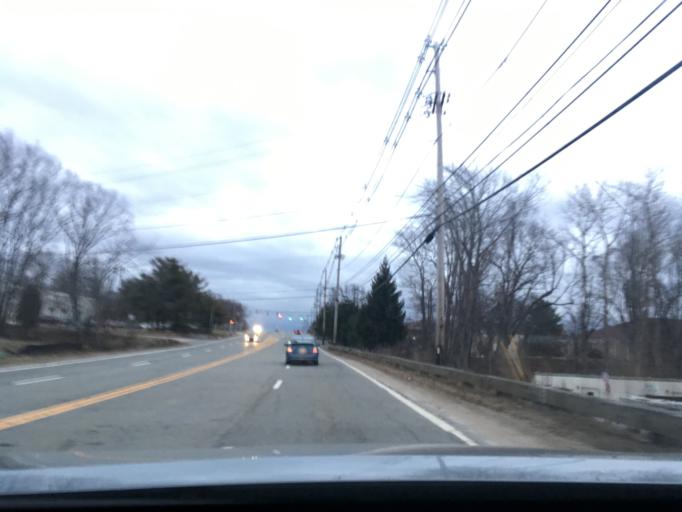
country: US
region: Rhode Island
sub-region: Providence County
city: Smithfield
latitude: 41.9141
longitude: -71.5177
